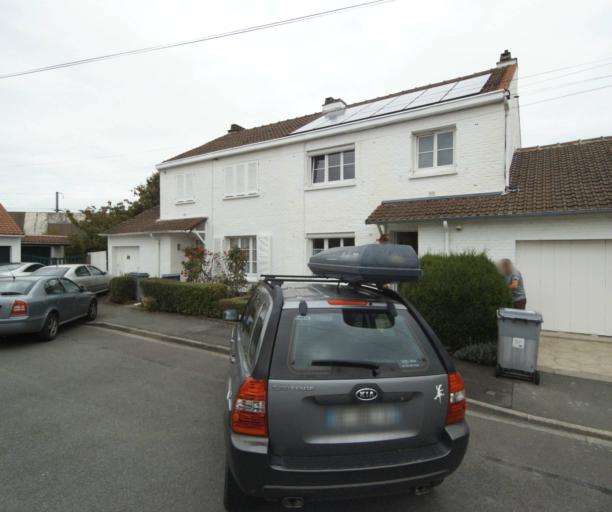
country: FR
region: Nord-Pas-de-Calais
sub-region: Departement du Nord
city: Lambersart
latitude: 50.6612
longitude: 3.0165
